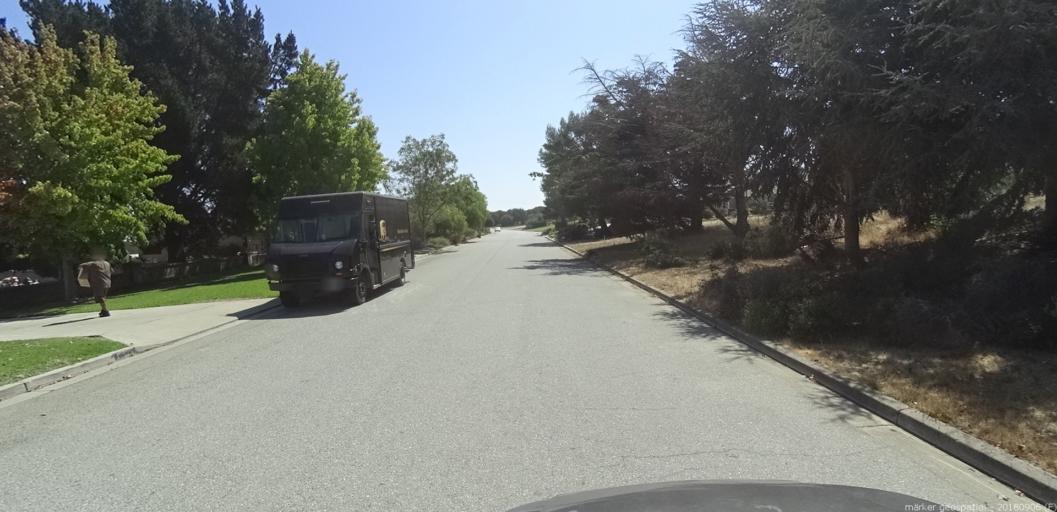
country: US
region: California
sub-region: Monterey County
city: Salinas
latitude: 36.5891
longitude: -121.6322
